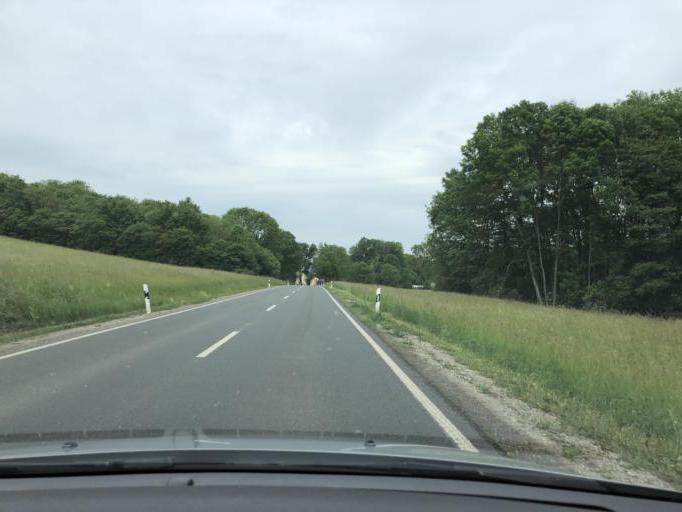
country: DE
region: Thuringia
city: Rannstedt
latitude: 51.0993
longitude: 11.5355
